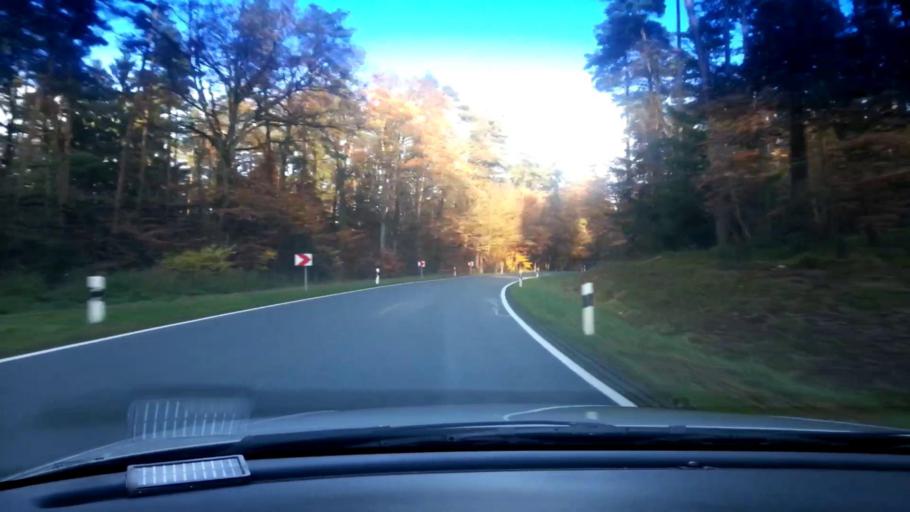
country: DE
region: Bavaria
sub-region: Upper Franconia
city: Strullendorf
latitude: 49.8633
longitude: 10.9803
